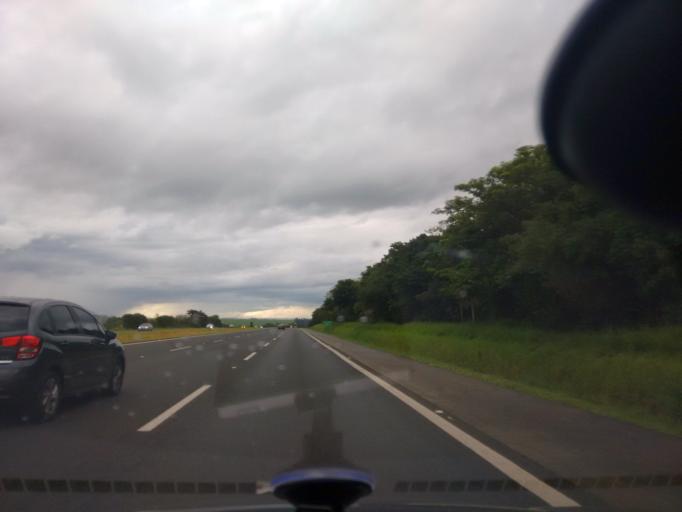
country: BR
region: Sao Paulo
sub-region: Santa Barbara D'Oeste
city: Santa Barbara d'Oeste
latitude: -22.8079
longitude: -47.3925
